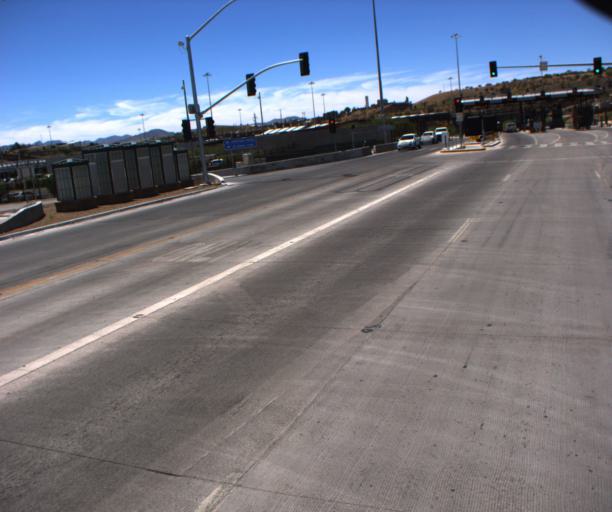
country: US
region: Arizona
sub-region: Santa Cruz County
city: Nogales
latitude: 31.3376
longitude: -110.9678
